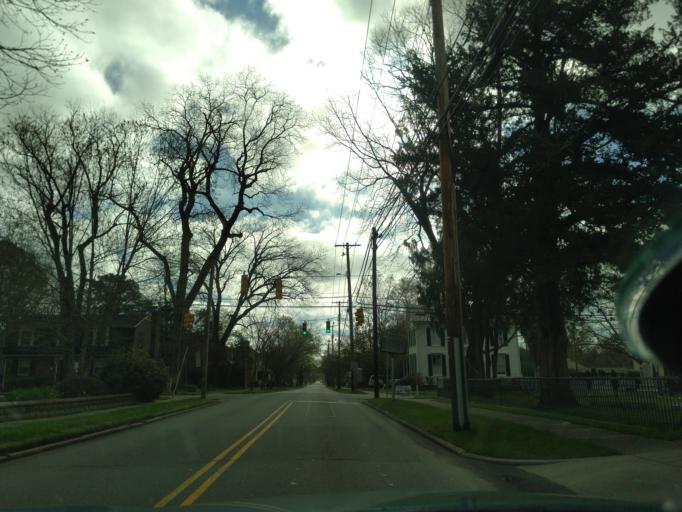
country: US
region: North Carolina
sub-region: Chowan County
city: Edenton
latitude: 36.0606
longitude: -76.6118
